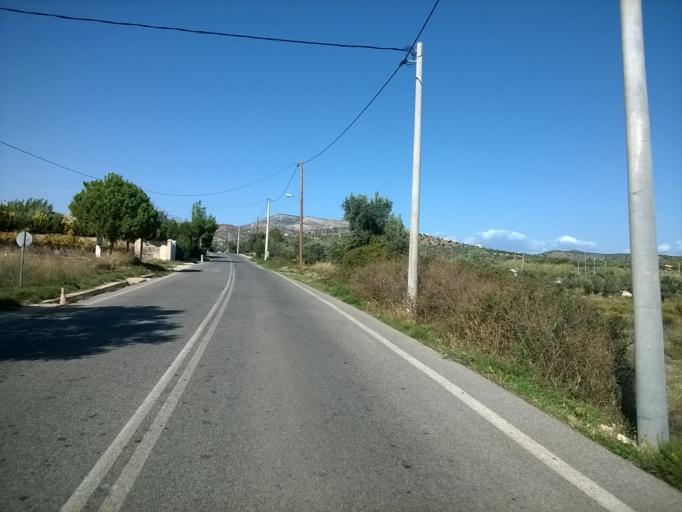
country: GR
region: Attica
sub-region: Nomarchia Anatolikis Attikis
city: Keratea
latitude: 37.7988
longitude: 23.9963
